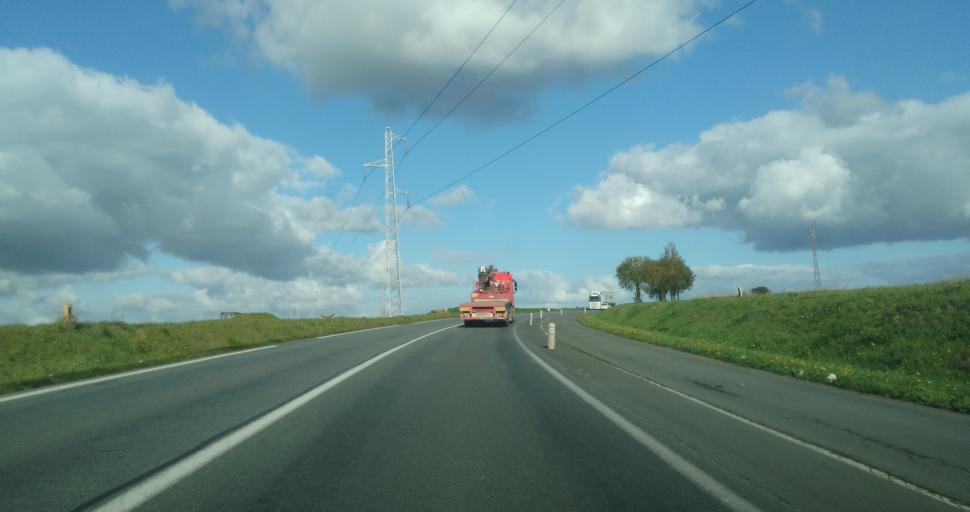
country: FR
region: Nord-Pas-de-Calais
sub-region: Departement du Pas-de-Calais
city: Maroeuil
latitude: 50.3144
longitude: 2.7205
